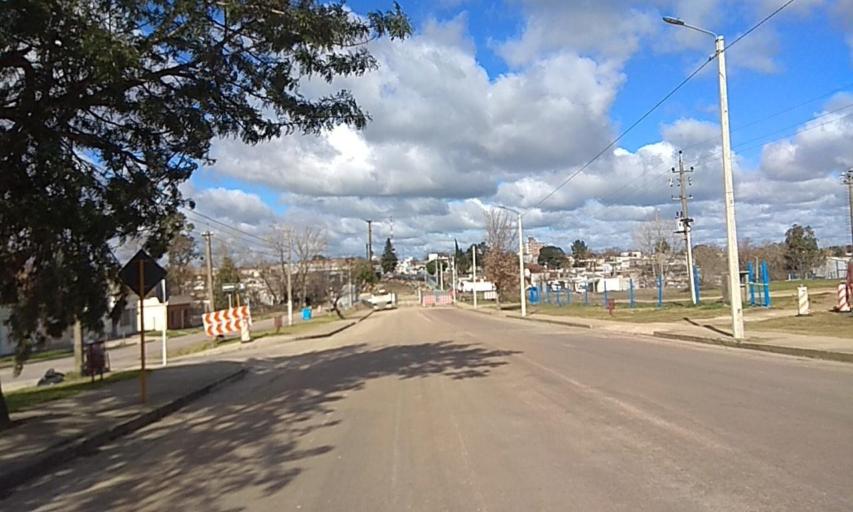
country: UY
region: Florida
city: Florida
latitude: -34.0883
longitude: -56.2218
